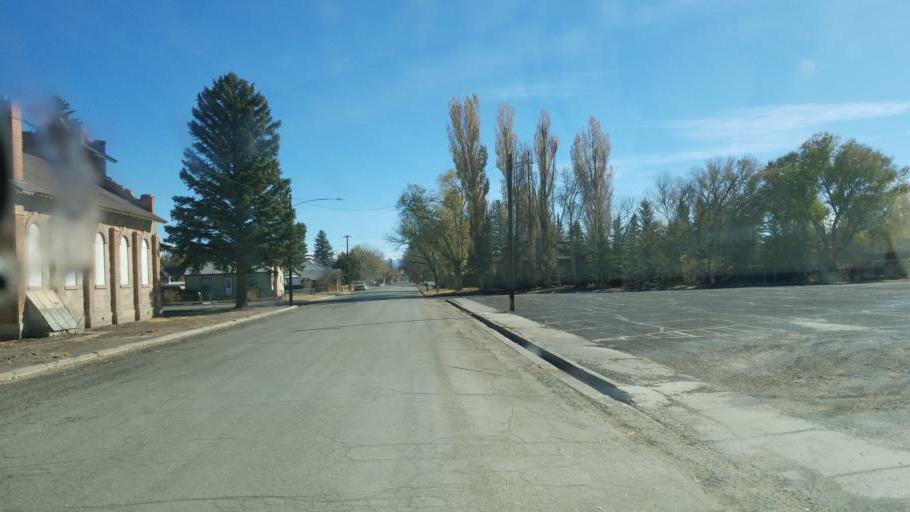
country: US
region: Colorado
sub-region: Rio Grande County
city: Monte Vista
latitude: 37.5766
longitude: -106.1517
